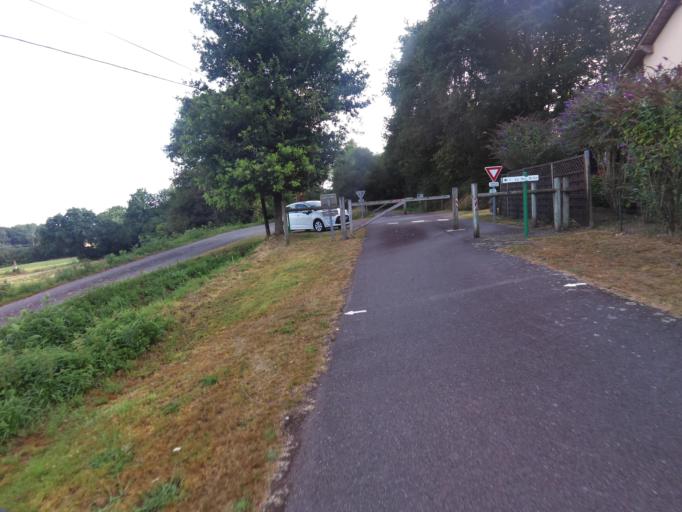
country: FR
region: Brittany
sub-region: Departement du Morbihan
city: Guillac
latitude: 47.9041
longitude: -2.4329
